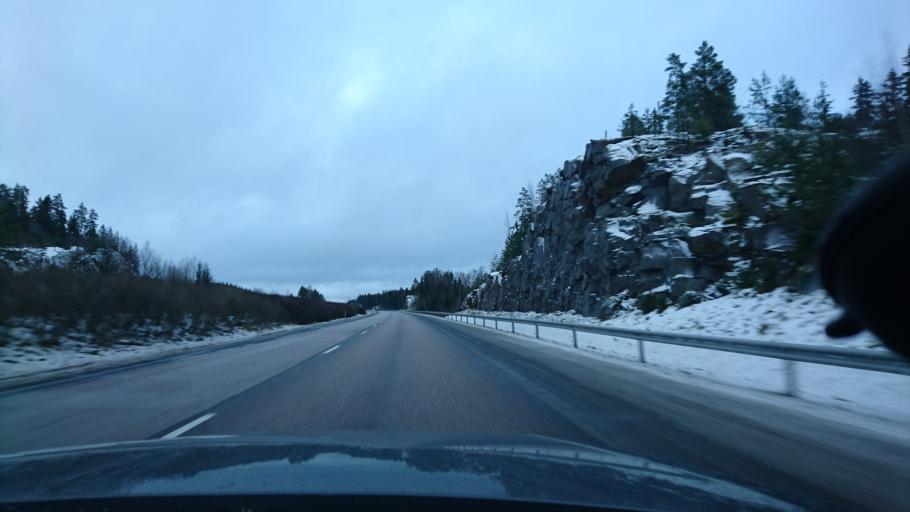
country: FI
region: Uusimaa
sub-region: Porvoo
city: Pukkila
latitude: 60.7211
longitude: 25.4370
